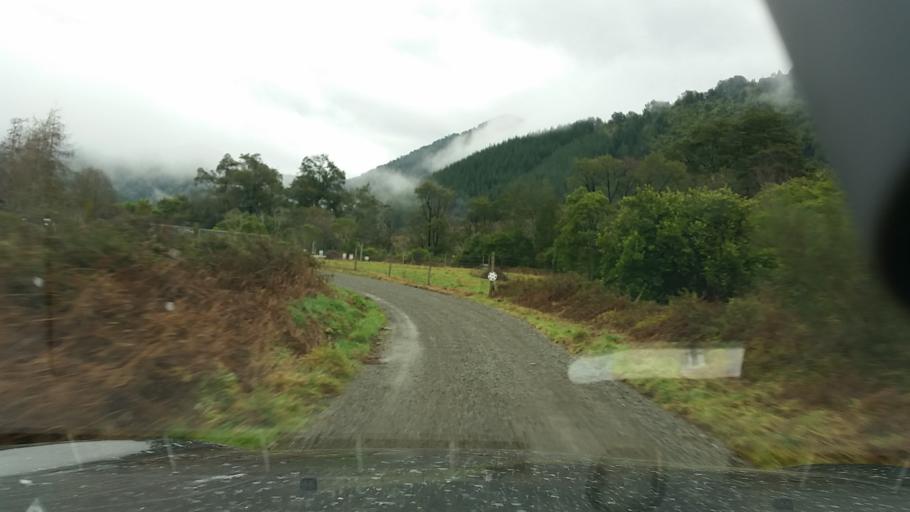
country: NZ
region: Nelson
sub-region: Nelson City
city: Nelson
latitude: -41.3559
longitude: 173.6237
